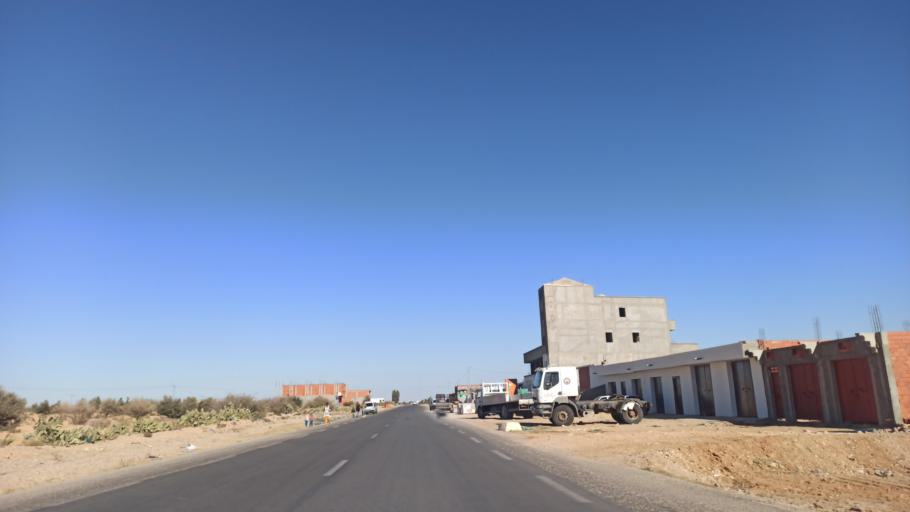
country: TN
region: Sidi Bu Zayd
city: Bi'r al Hufayy
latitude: 34.9487
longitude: 9.2102
